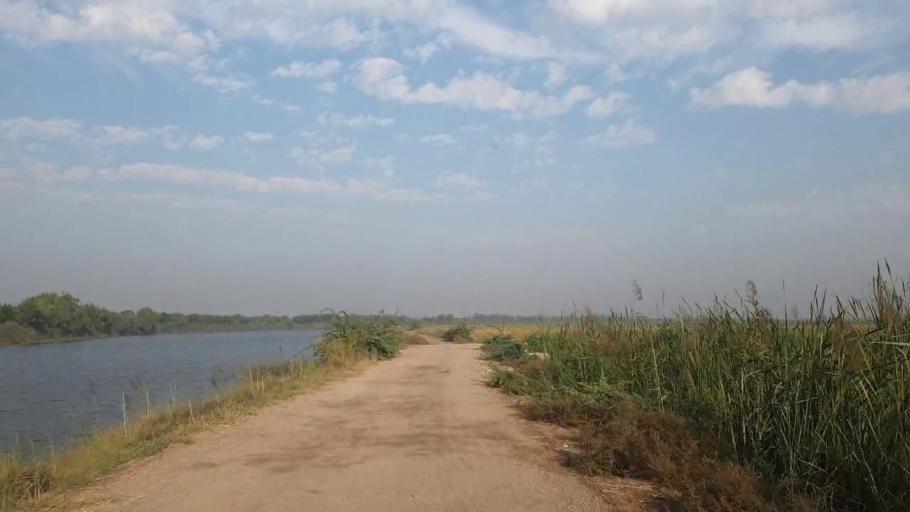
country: PK
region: Sindh
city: Tando Bago
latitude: 24.8170
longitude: 68.9542
